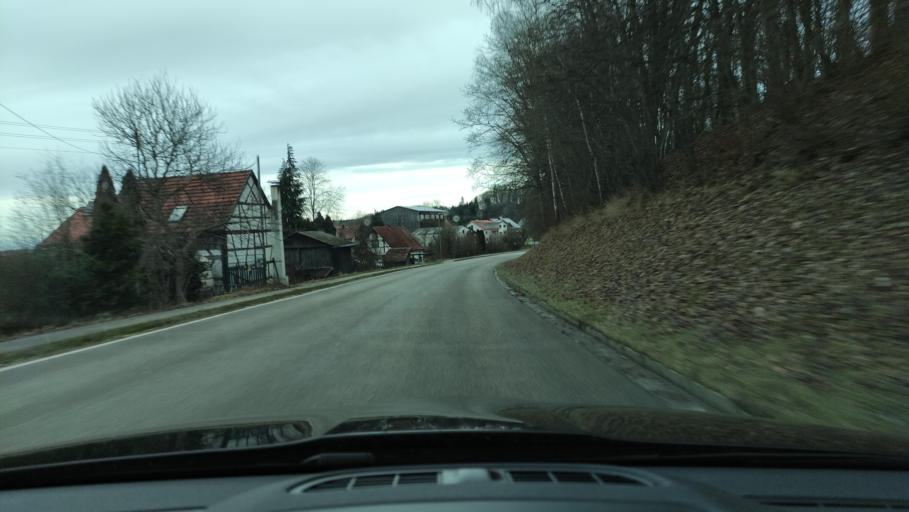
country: DE
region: Bavaria
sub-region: Swabia
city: Buch
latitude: 48.2423
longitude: 10.2112
